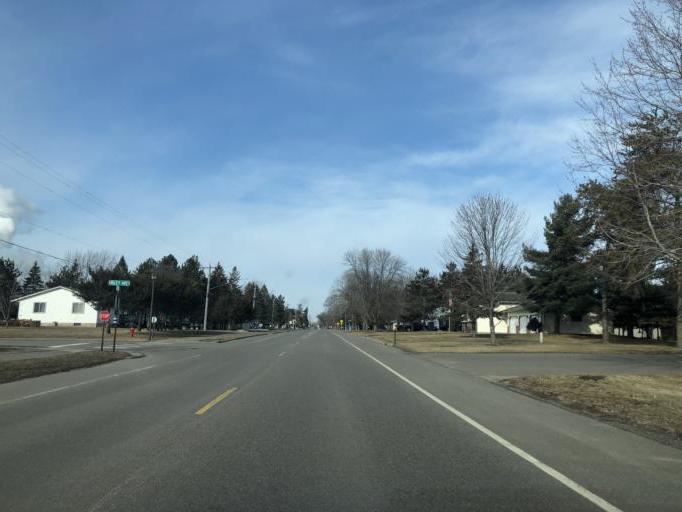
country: US
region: Minnesota
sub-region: Sherburne County
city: Becker
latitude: 45.3937
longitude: -93.8645
